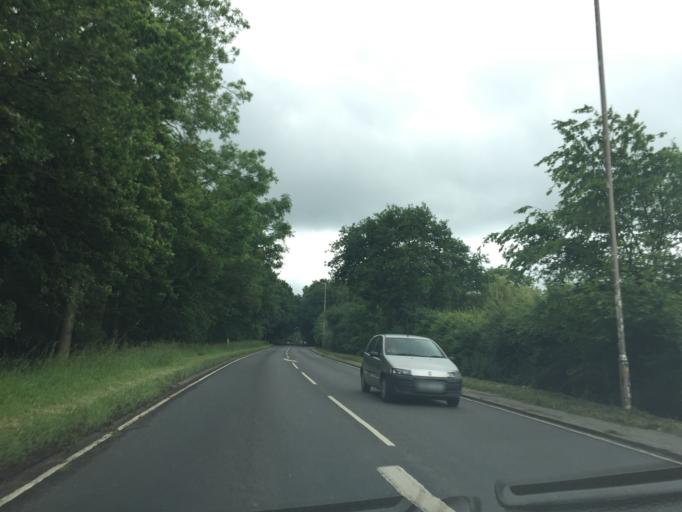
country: GB
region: England
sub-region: Essex
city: Epping
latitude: 51.7099
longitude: 0.1237
